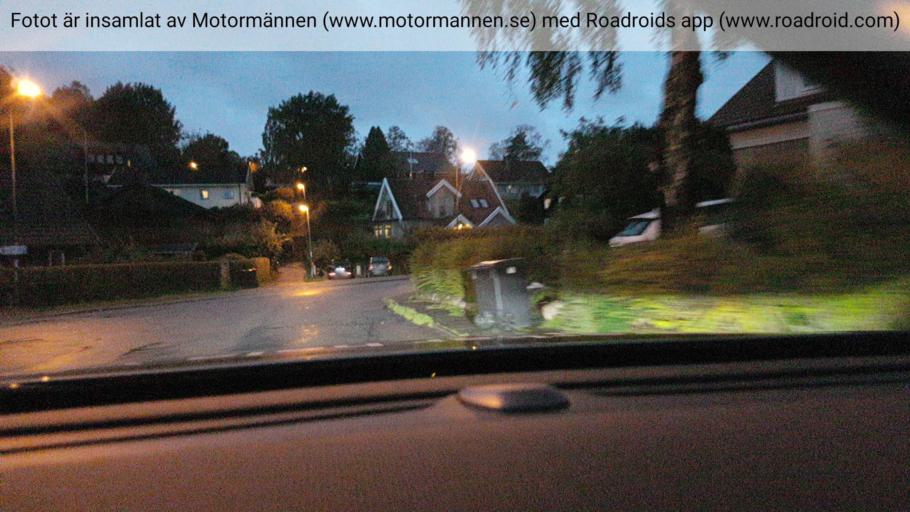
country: SE
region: Vaestra Goetaland
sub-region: Molndal
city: Moelndal
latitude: 57.6733
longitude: 11.9929
